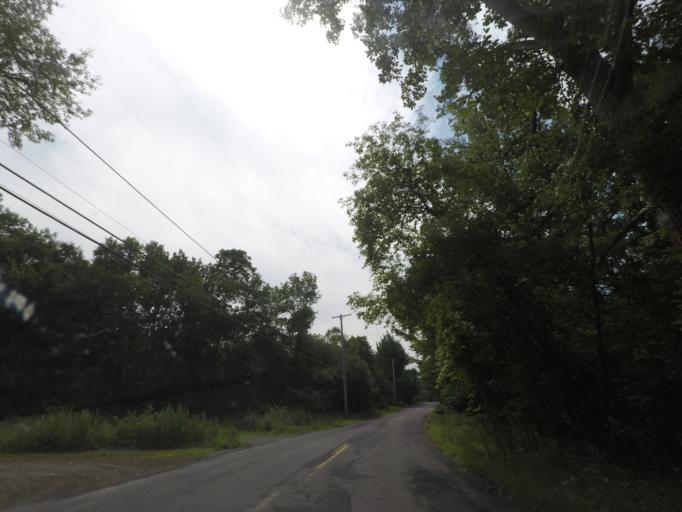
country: US
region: New York
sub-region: Rensselaer County
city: Wynantskill
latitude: 42.7537
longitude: -73.6070
